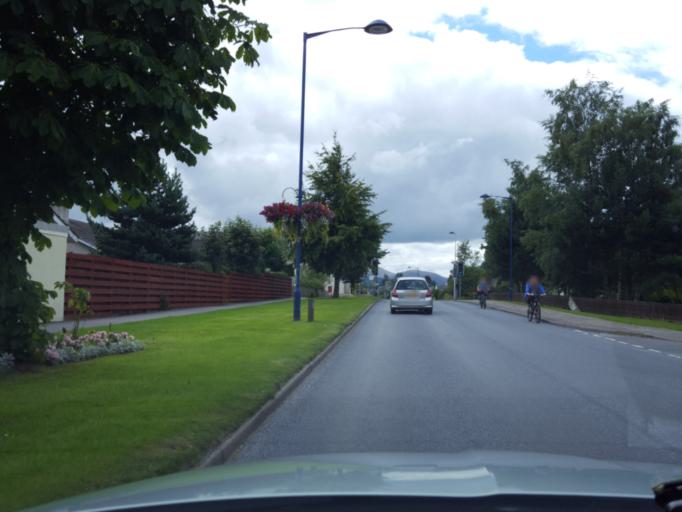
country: GB
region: Scotland
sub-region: Highland
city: Aviemore
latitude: 57.1993
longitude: -3.8286
